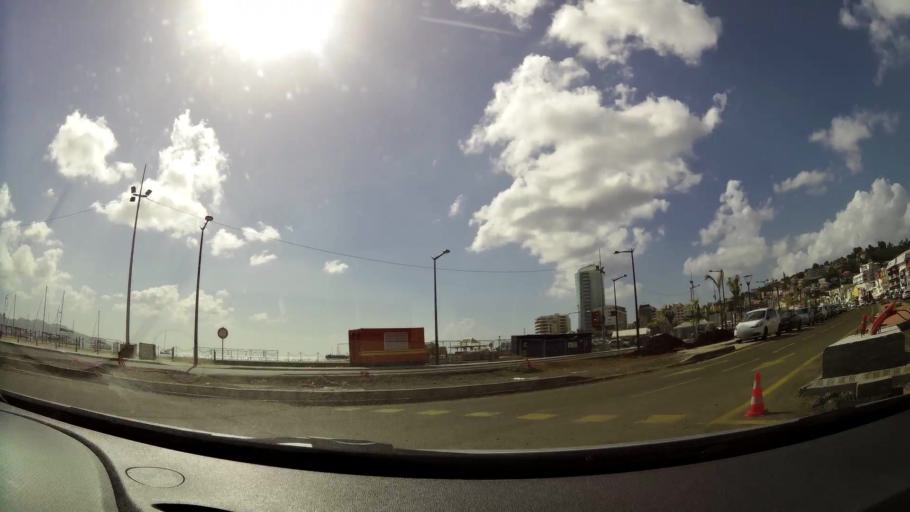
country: MQ
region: Martinique
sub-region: Martinique
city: Fort-de-France
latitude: 14.6027
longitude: -61.0693
